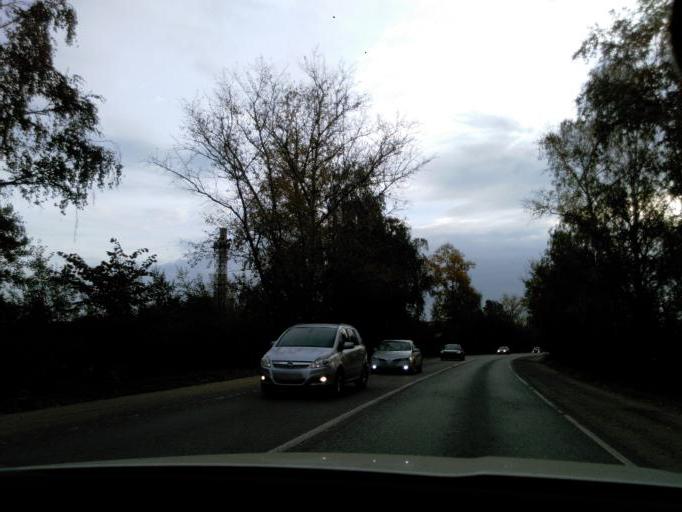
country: RU
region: Moskovskaya
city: Sheremet'yevskiy
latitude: 55.9723
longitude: 37.4861
